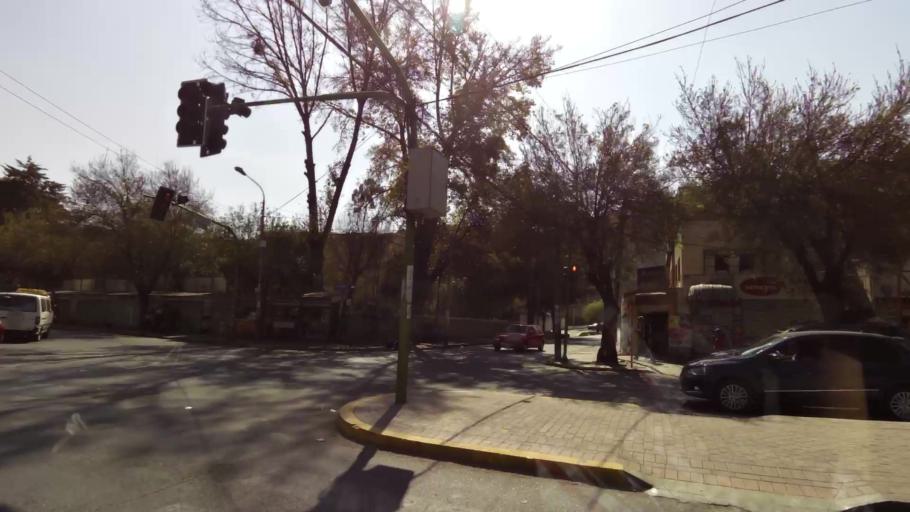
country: BO
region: La Paz
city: La Paz
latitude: -16.5412
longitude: -68.0914
